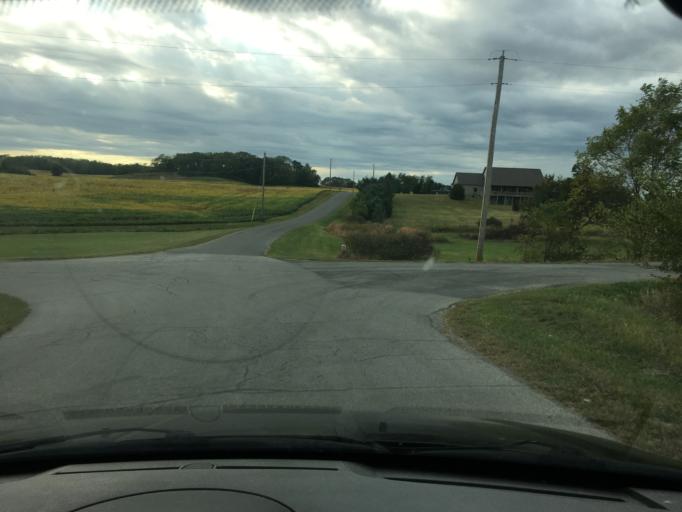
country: US
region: Ohio
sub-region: Logan County
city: Bellefontaine
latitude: 40.3347
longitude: -83.8046
